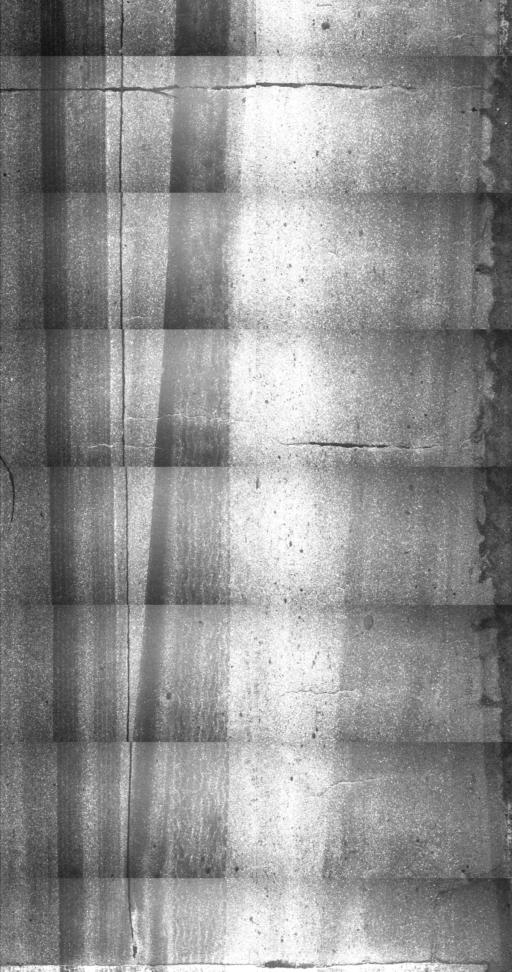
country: US
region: Vermont
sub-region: Orange County
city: Randolph
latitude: 43.8741
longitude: -72.6475
